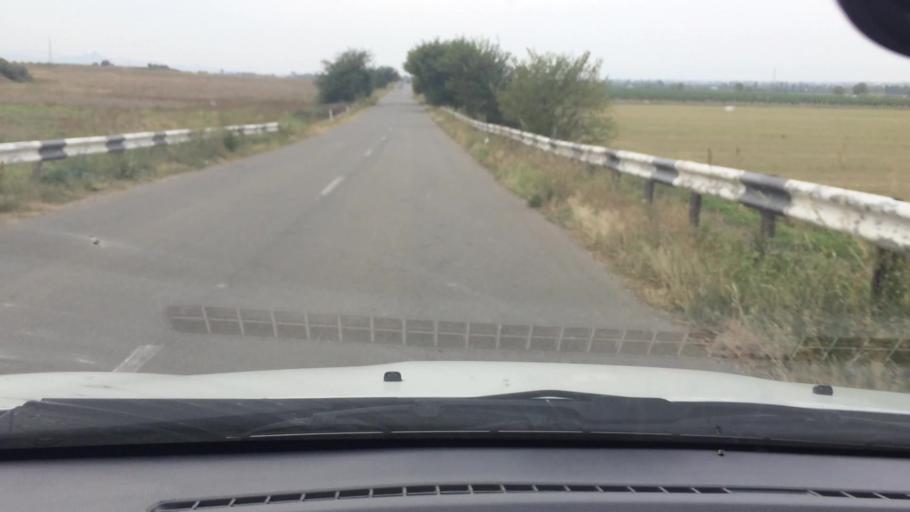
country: AM
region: Tavush
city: Berdavan
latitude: 41.3416
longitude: 44.9927
